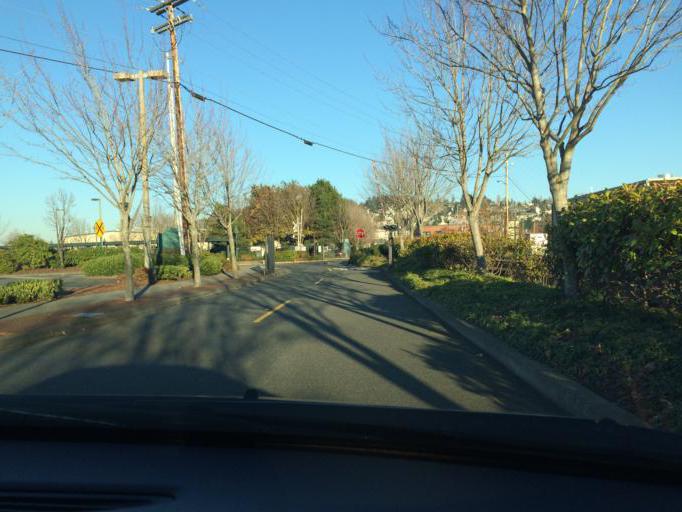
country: US
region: Washington
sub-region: Whatcom County
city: Bellingham
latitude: 48.7199
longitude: -122.5136
